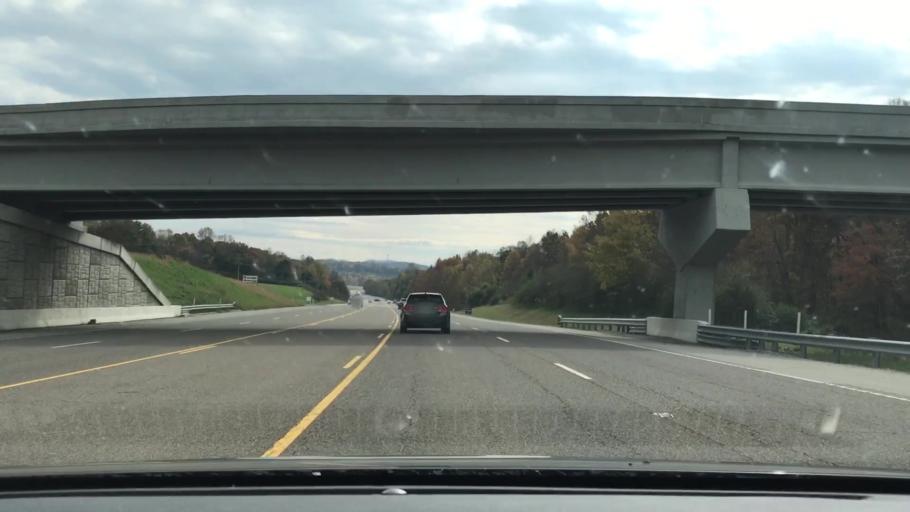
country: US
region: Tennessee
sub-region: Scott County
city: Oneida
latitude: 36.4590
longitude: -84.5476
